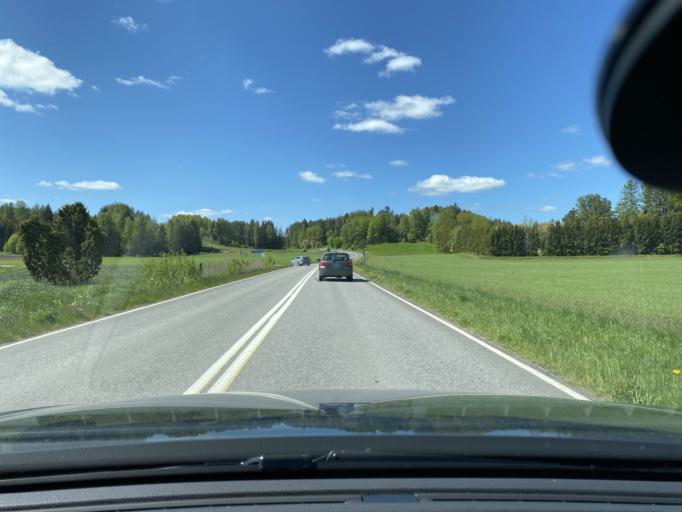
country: FI
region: Varsinais-Suomi
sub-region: Salo
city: Halikko
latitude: 60.3655
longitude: 22.9987
